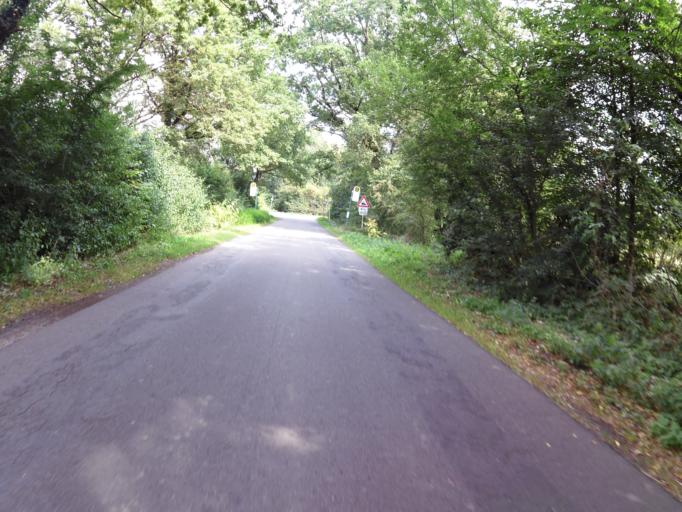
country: DE
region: Lower Saxony
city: Nienburg
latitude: 52.6095
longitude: 9.1933
